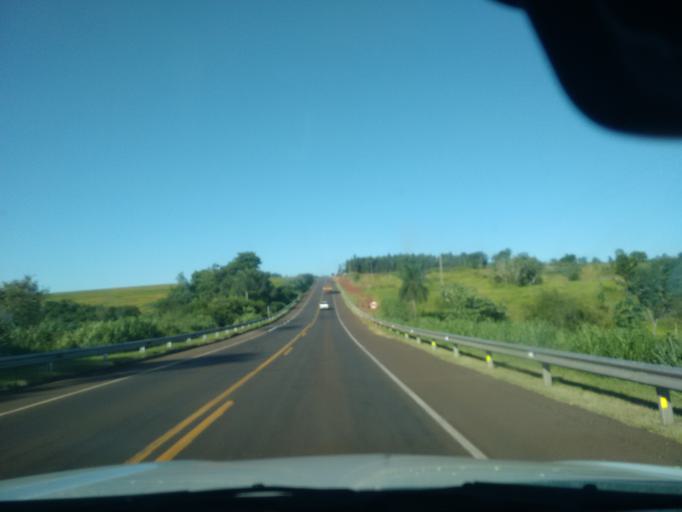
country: PY
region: Canindeyu
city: Salto del Guaira
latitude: -23.9661
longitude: -54.3258
